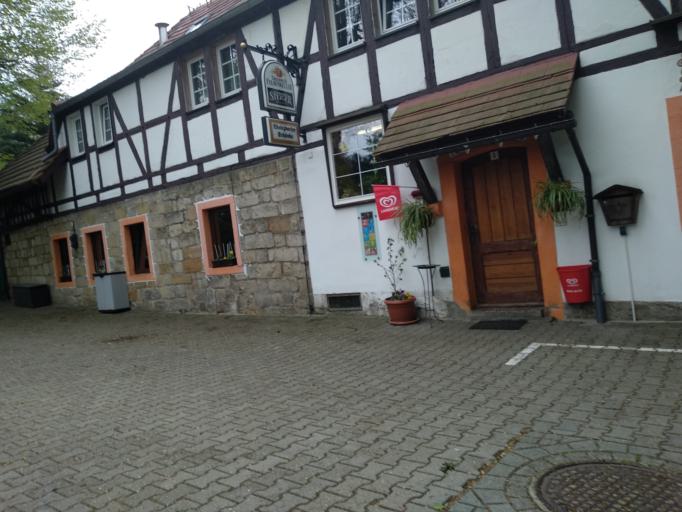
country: DE
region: Saxony
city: Porschdorf
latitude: 50.9557
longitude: 14.1383
